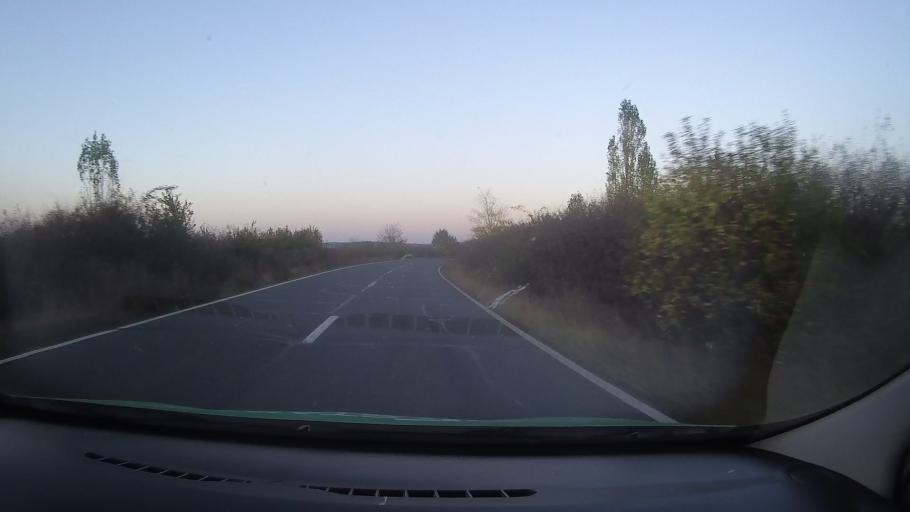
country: RO
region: Timis
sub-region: Comuna Dumbrava
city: Dumbrava
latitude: 45.8352
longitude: 22.1391
